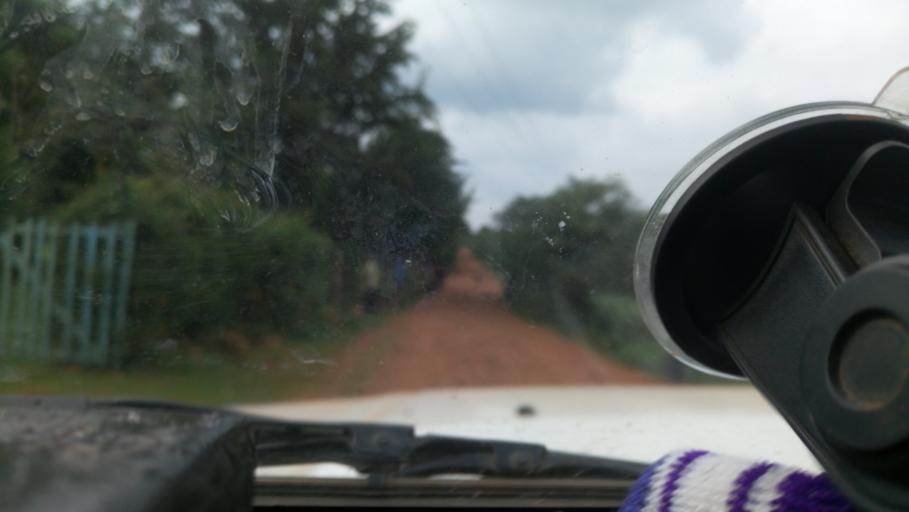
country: KE
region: Kericho
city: Litein
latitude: -0.5834
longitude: 35.2061
